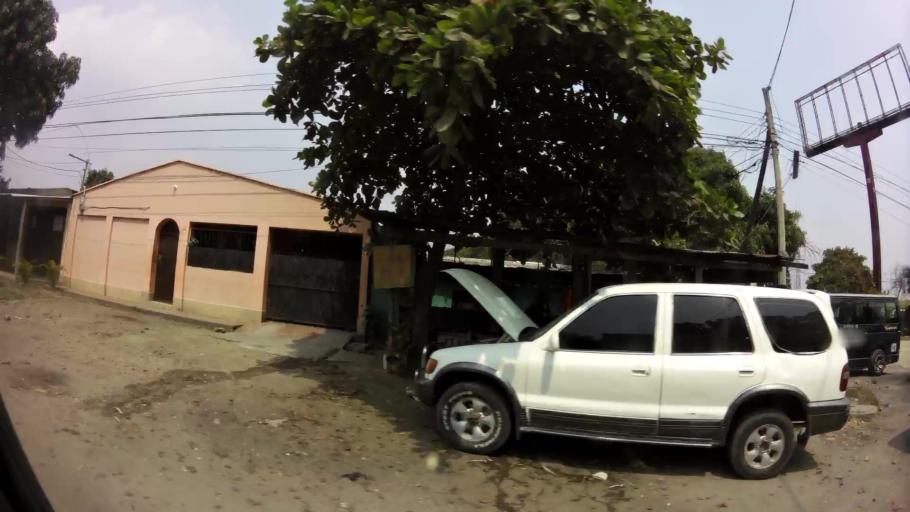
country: HN
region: Cortes
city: San Pedro Sula
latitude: 15.4825
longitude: -88.0072
